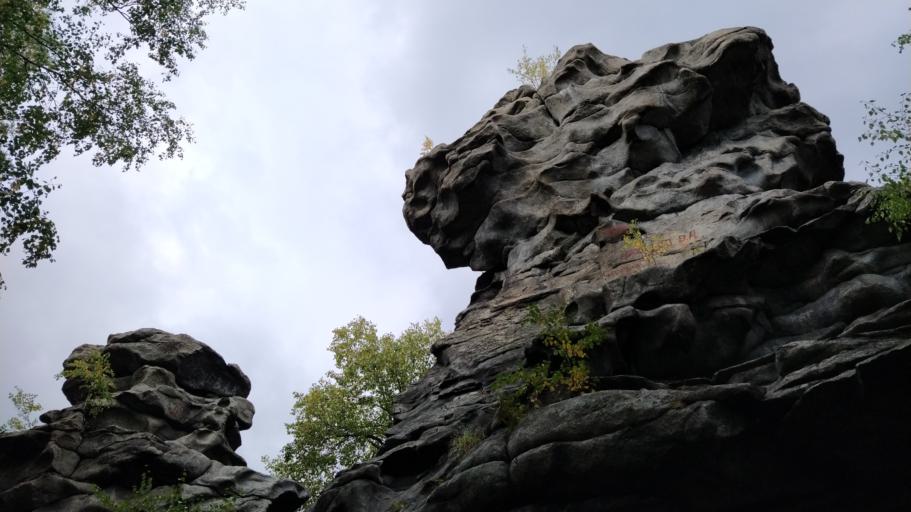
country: RU
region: Sverdlovsk
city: Verkh-Neyvinskiy
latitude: 57.2405
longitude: 60.2297
